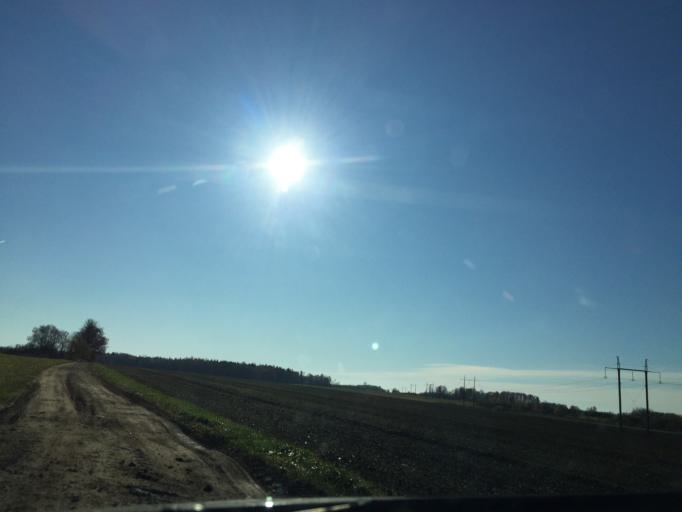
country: LV
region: Skriveri
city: Skriveri
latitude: 56.6676
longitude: 25.1699
